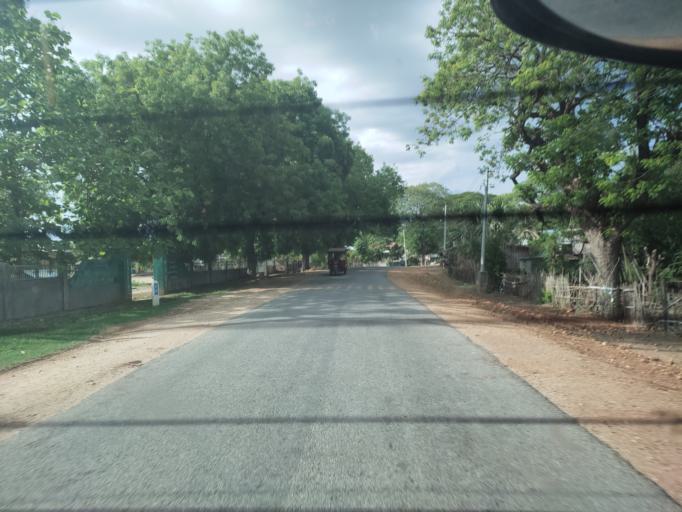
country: MM
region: Magway
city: Magway
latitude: 19.9948
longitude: 94.9888
